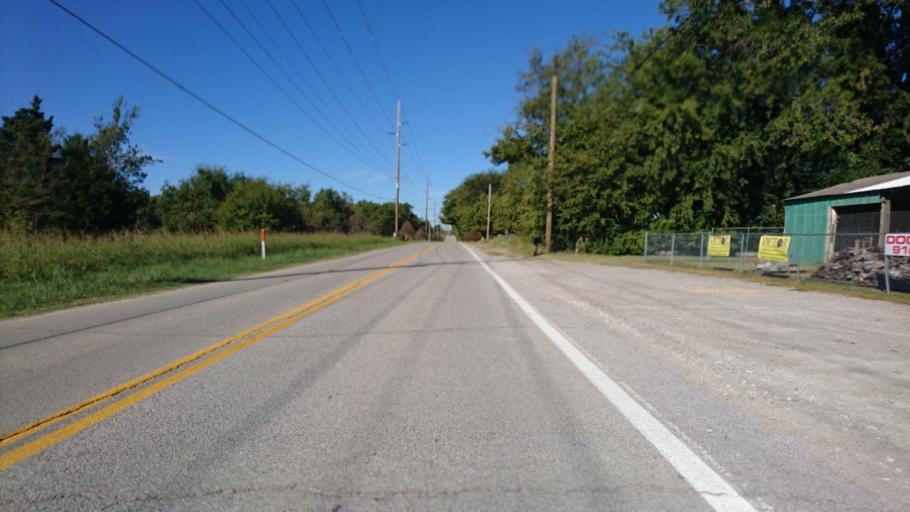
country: US
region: Oklahoma
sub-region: Rogers County
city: Catoosa
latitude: 36.1480
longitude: -95.7652
